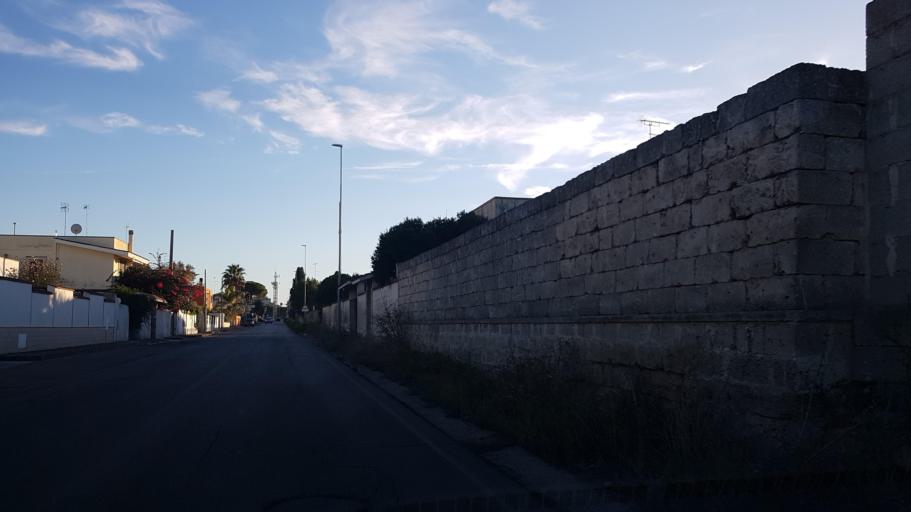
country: IT
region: Apulia
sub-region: Provincia di Lecce
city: Lecce
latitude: 40.3734
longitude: 18.1795
